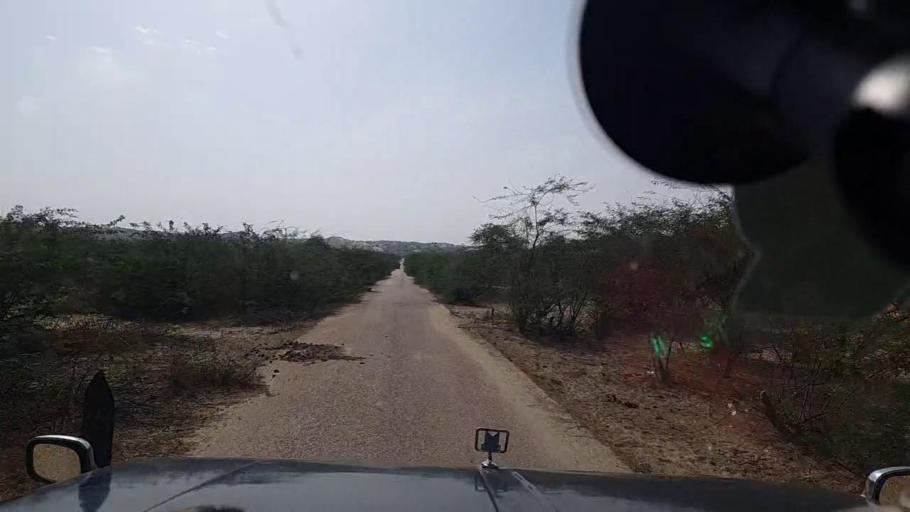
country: PK
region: Sindh
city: Diplo
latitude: 24.4199
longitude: 69.4714
